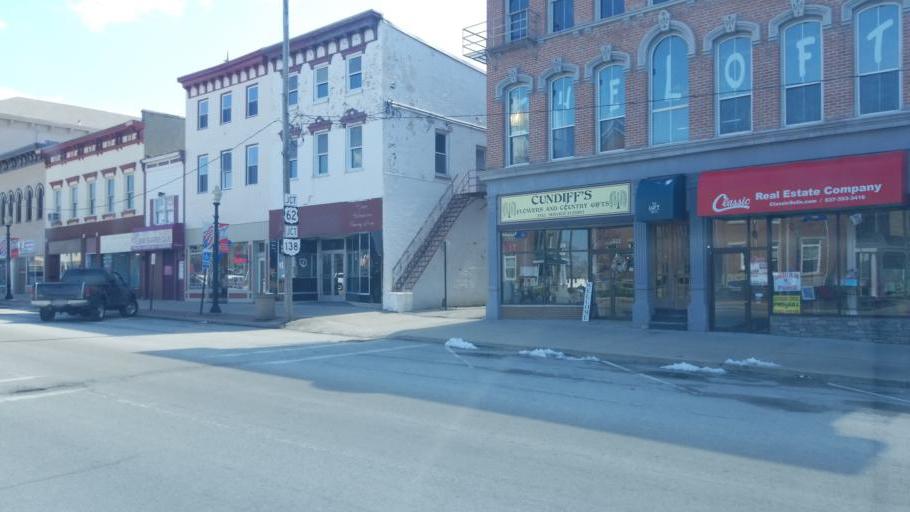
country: US
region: Ohio
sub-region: Highland County
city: Hillsboro
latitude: 39.2024
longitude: -83.6126
